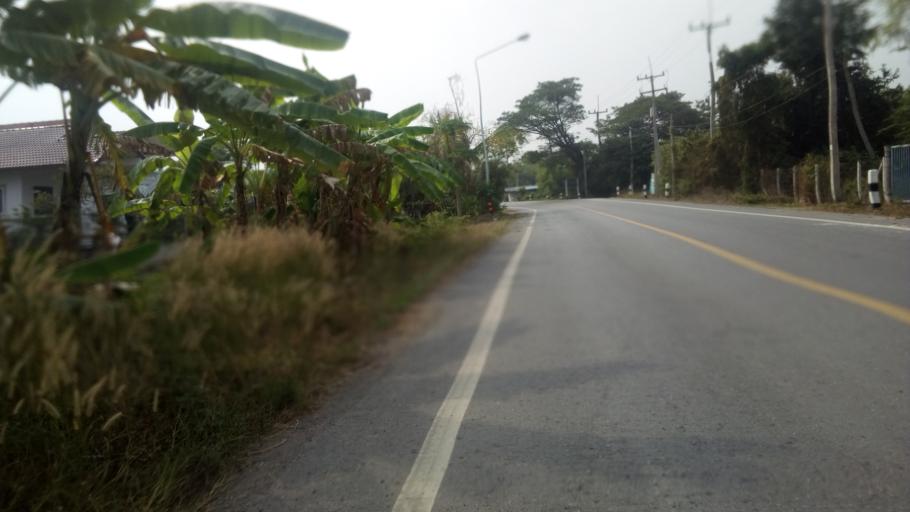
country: TH
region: Pathum Thani
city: Ban Rangsit
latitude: 14.0371
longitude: 100.8242
